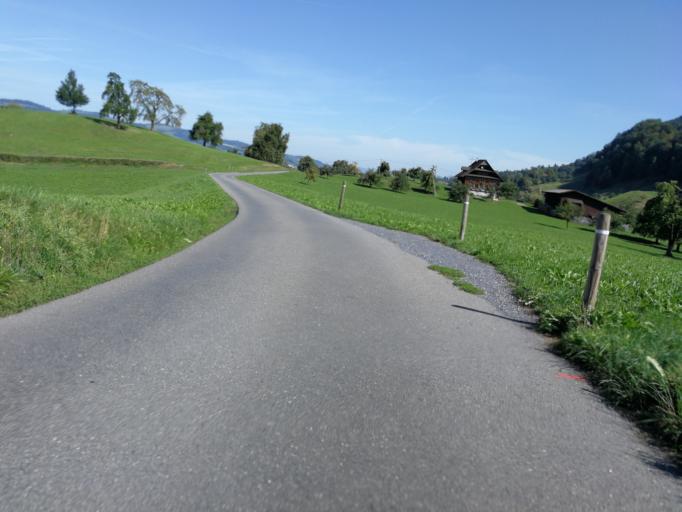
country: CH
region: Lucerne
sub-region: Lucerne-Land District
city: Weggis
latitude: 47.0436
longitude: 8.4273
